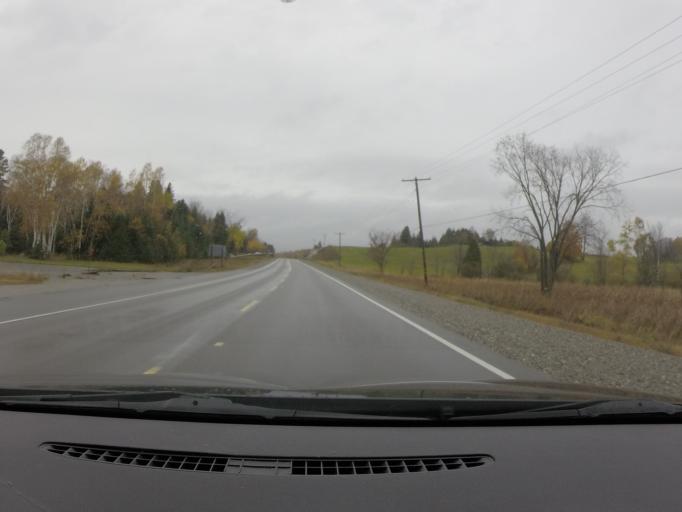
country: CA
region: Ontario
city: Skatepark
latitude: 44.7548
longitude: -76.8558
